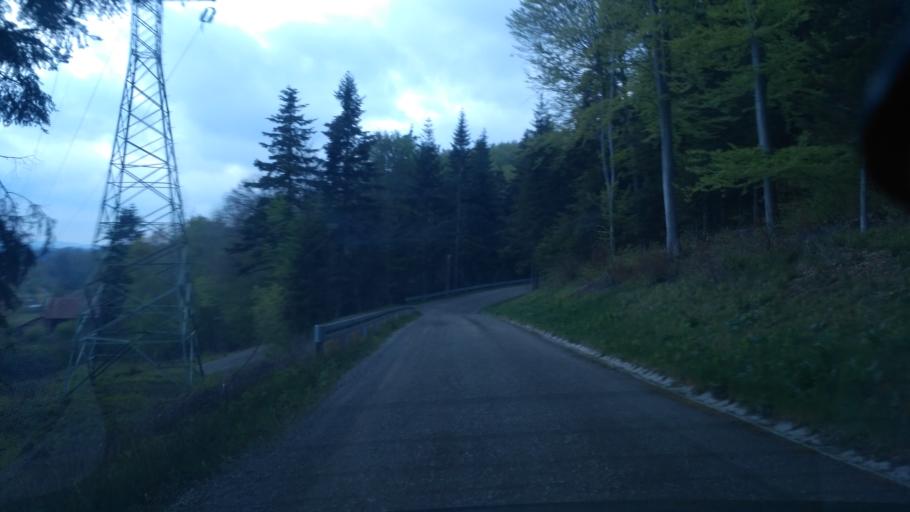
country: PL
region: Subcarpathian Voivodeship
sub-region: Powiat sanocki
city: Sanok
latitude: 49.5701
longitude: 22.2274
